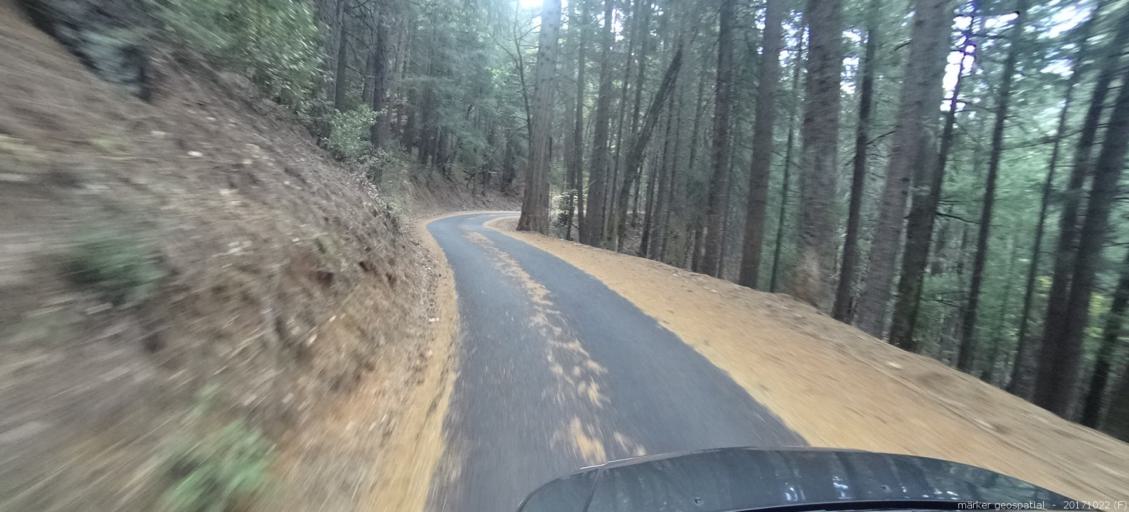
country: US
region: California
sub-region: Siskiyou County
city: Dunsmuir
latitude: 41.1597
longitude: -122.2895
